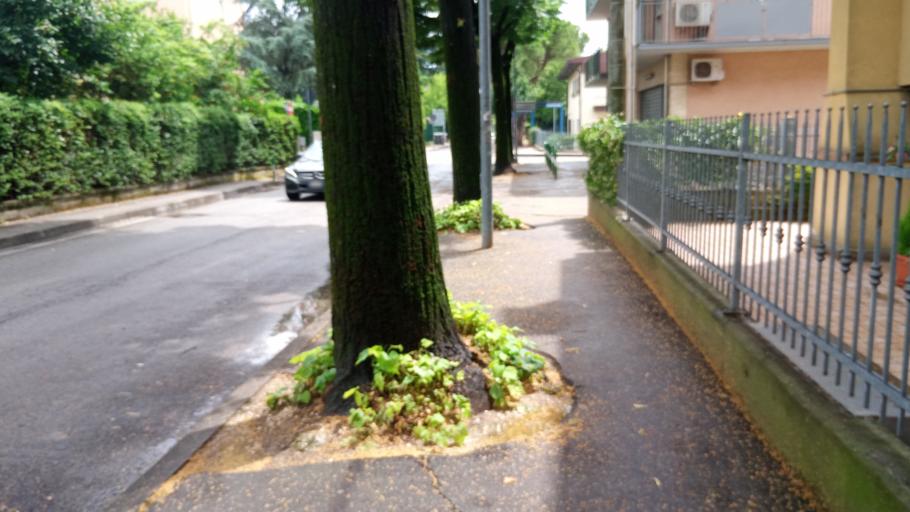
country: IT
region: Veneto
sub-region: Provincia di Padova
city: Padova
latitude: 45.4297
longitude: 11.8918
